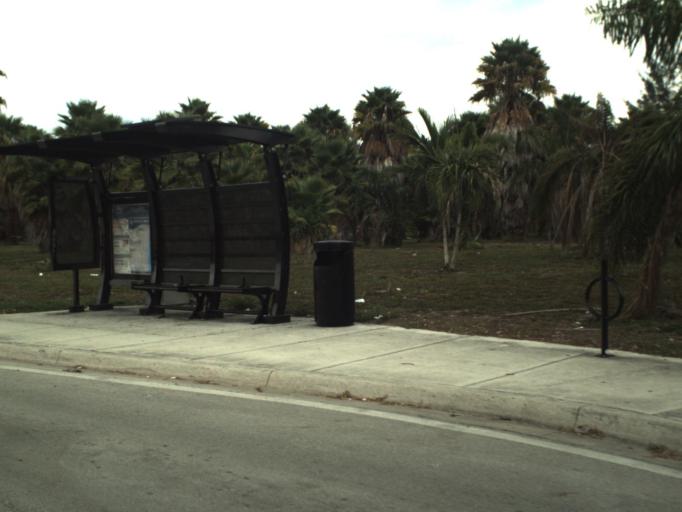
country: US
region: Florida
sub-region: Broward County
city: Dania Beach
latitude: 26.0486
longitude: -80.1494
